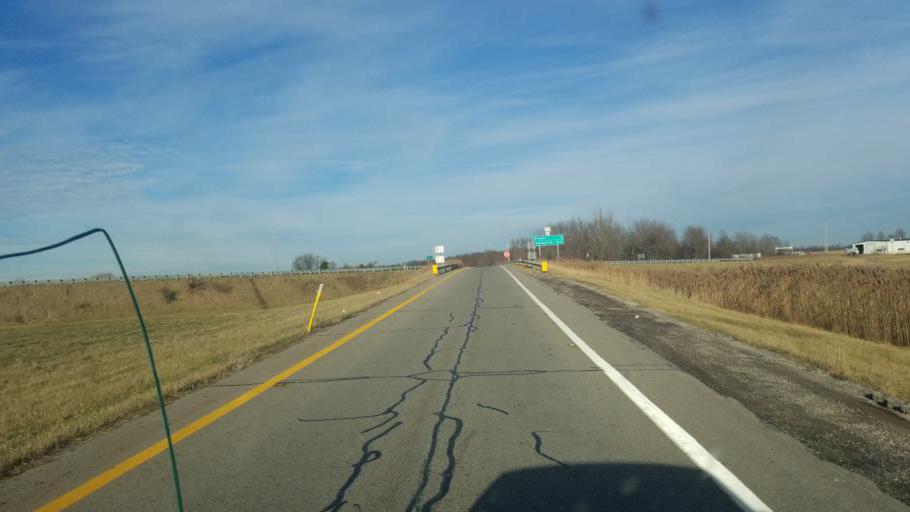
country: US
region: Ohio
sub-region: Ashtabula County
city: Roaming Shores
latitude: 41.5344
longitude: -80.7127
